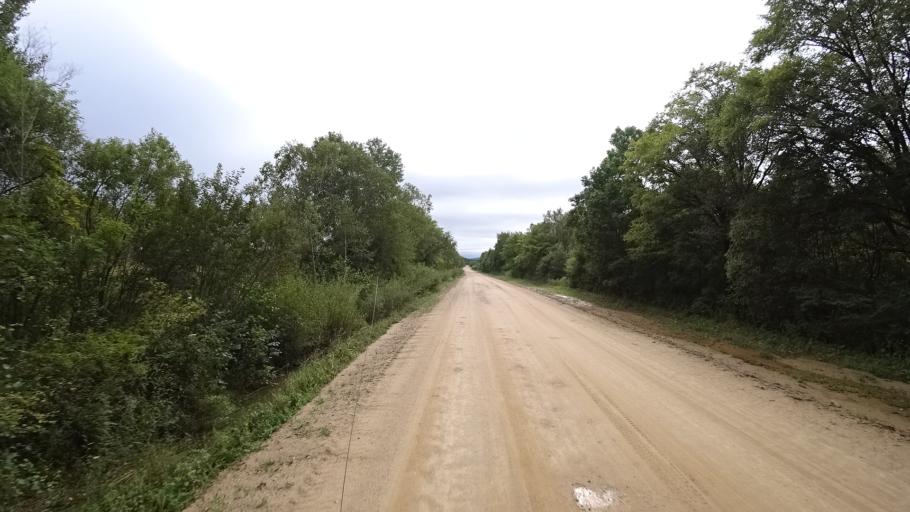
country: RU
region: Primorskiy
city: Monastyrishche
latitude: 44.1071
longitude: 132.6146
